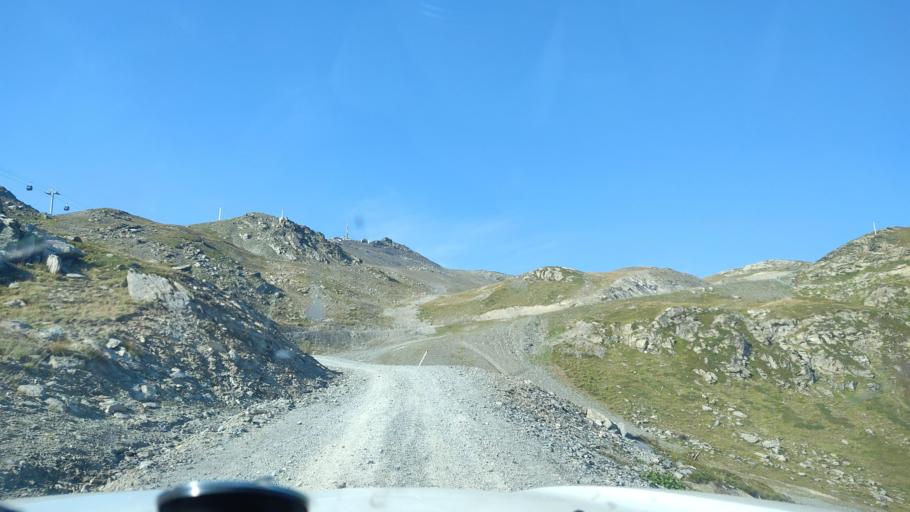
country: FR
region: Rhone-Alpes
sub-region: Departement de la Savoie
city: Val Thorens
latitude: 45.3056
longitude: 6.5164
